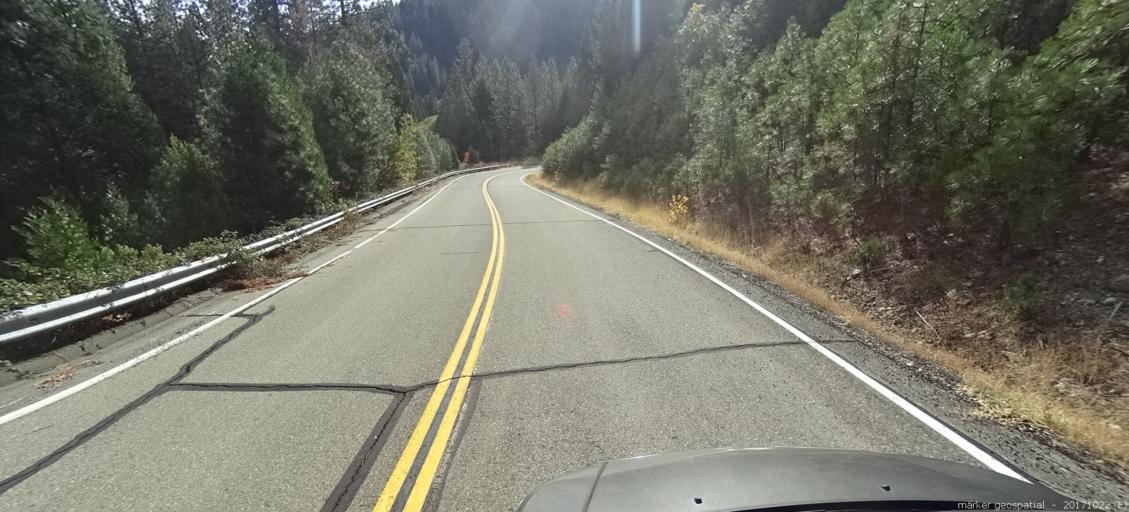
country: US
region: California
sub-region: Siskiyou County
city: Dunsmuir
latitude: 41.0614
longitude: -122.3723
